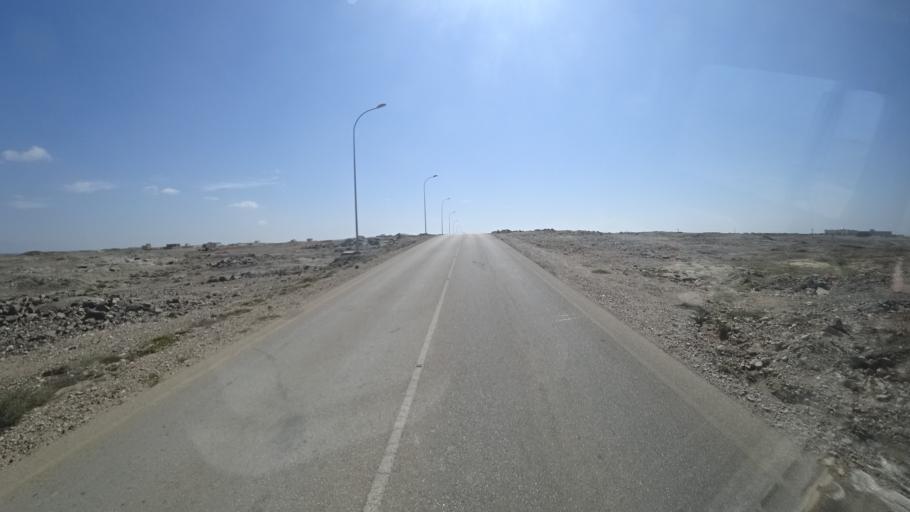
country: OM
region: Zufar
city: Salalah
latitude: 16.9680
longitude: 54.7320
